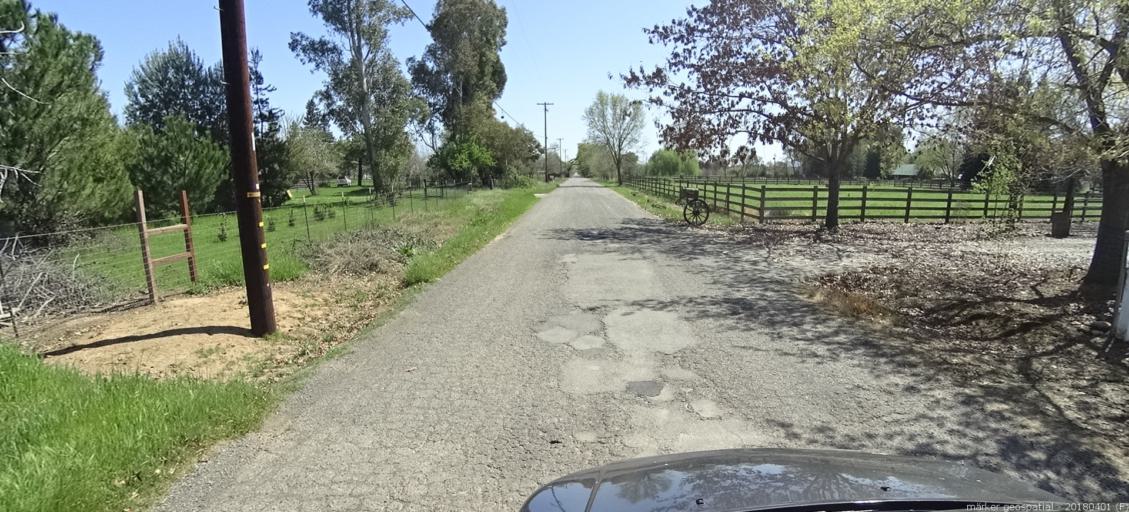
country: US
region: California
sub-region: Sacramento County
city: Rancho Murieta
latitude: 38.4546
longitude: -121.1777
